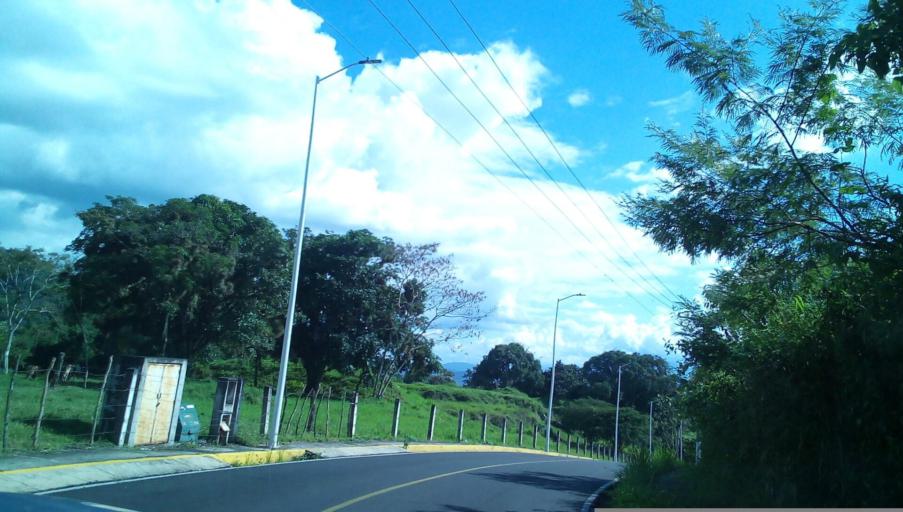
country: MX
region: Veracruz
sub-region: Cordoba
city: El Porvenir
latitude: 18.9051
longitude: -96.9230
